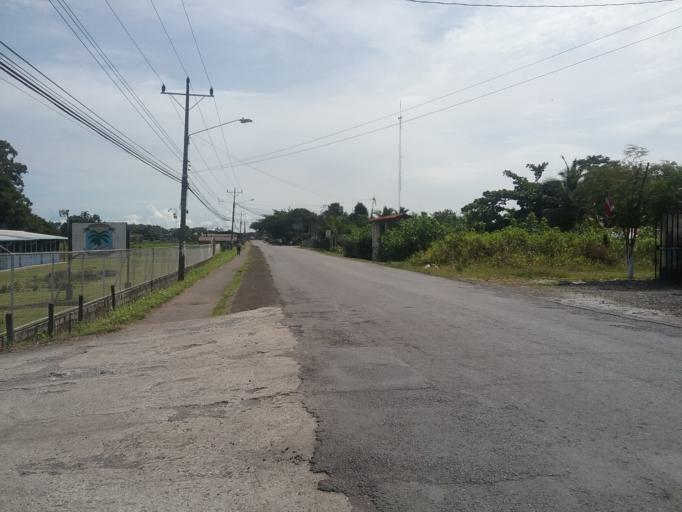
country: CR
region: Limon
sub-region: Canton de Pococi
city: Guapiles
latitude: 10.3204
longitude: -83.9063
